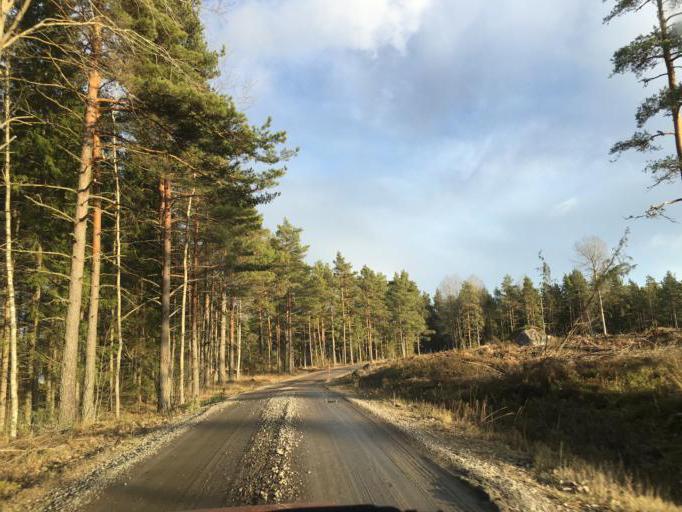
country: SE
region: Kalmar
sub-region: Vasterviks Kommun
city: Vaestervik
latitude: 57.6335
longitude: 16.5615
